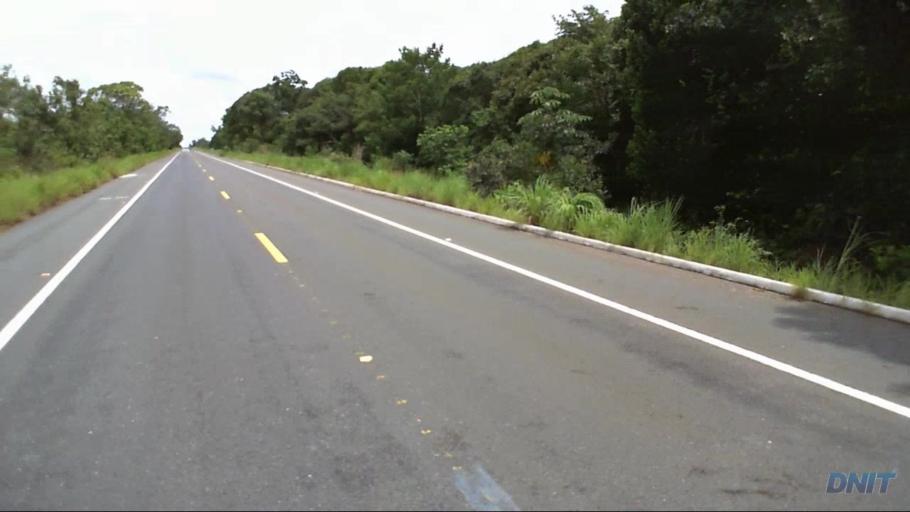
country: BR
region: Goias
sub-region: Sao Miguel Do Araguaia
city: Sao Miguel do Araguaia
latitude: -13.2867
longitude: -50.4688
